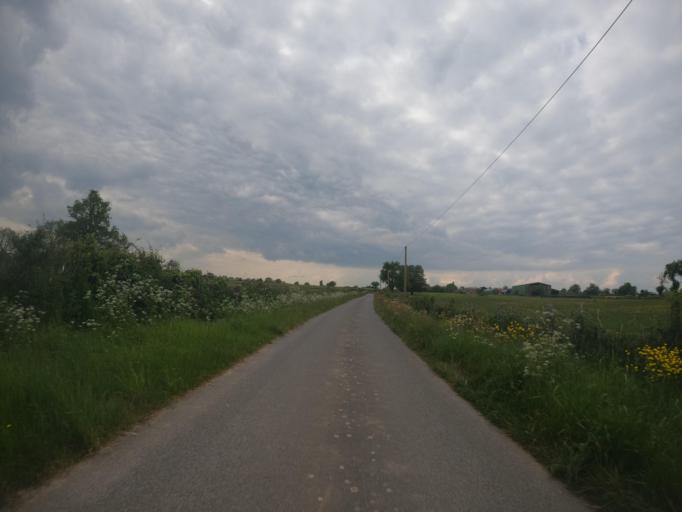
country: FR
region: Poitou-Charentes
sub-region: Departement des Deux-Sevres
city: Chiche
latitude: 46.8559
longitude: -0.3240
